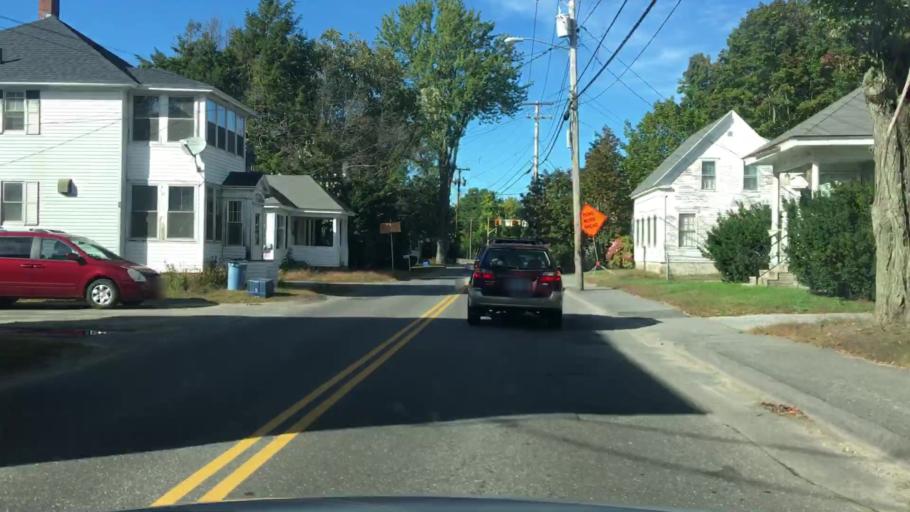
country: US
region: Maine
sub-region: Cumberland County
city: Brunswick
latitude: 43.9115
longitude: -69.9761
